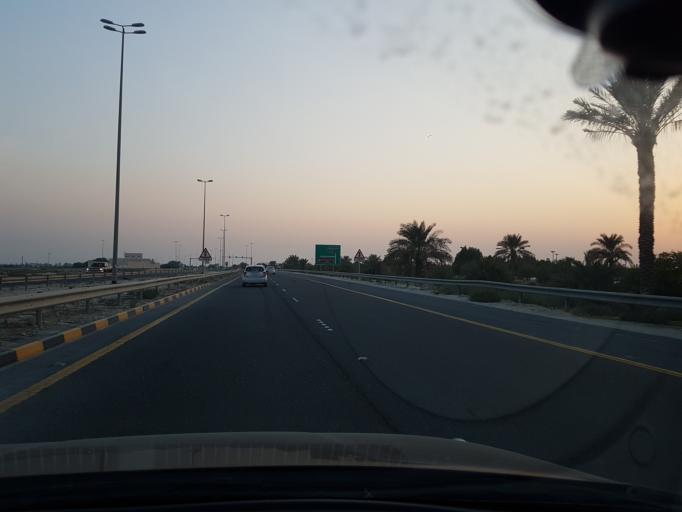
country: BH
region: Central Governorate
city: Dar Kulayb
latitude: 26.0269
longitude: 50.4955
